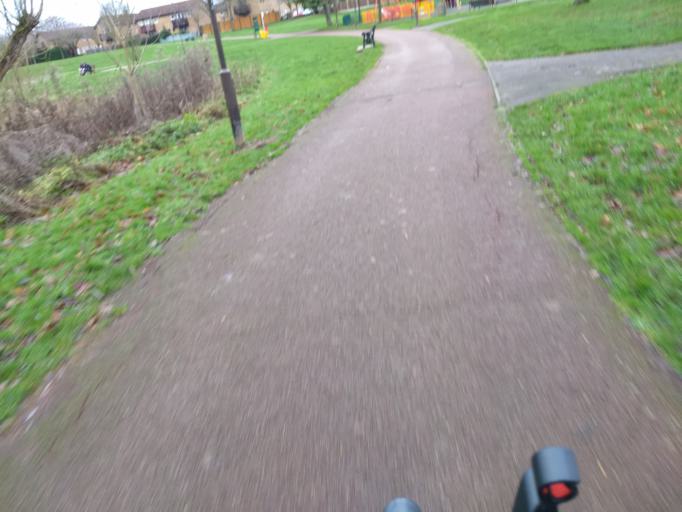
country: GB
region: England
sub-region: Buckinghamshire
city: Newton Longville
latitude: 51.9846
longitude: -0.7661
